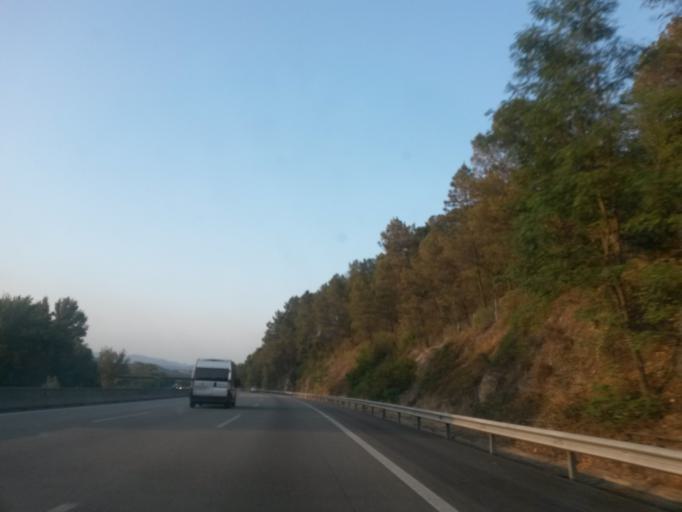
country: ES
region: Catalonia
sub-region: Provincia de Barcelona
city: Sant Celoni
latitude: 41.6936
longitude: 2.5112
